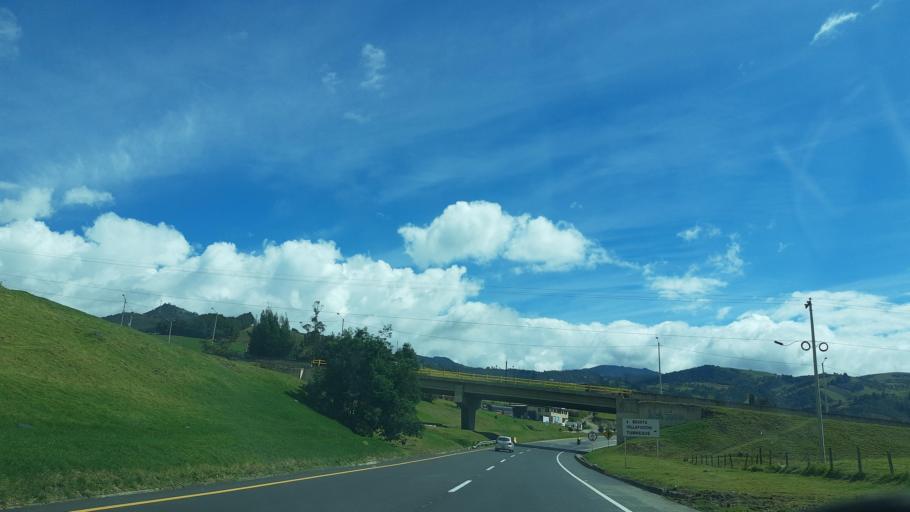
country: CO
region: Cundinamarca
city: Villapinzon
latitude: 5.2254
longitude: -73.5919
